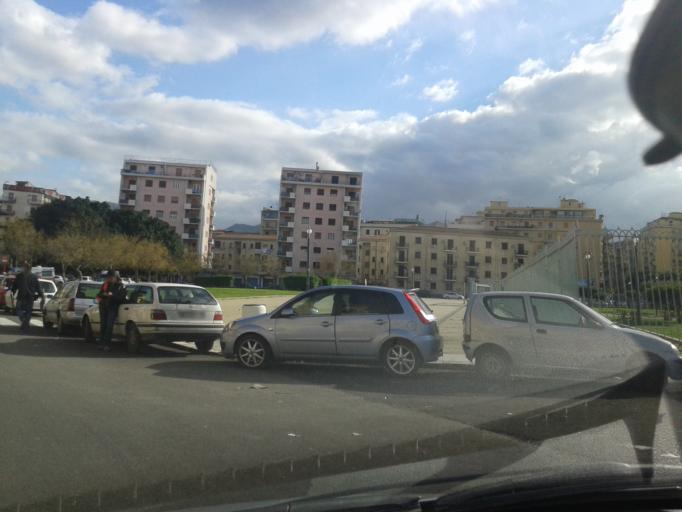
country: IT
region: Sicily
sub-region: Palermo
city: Palermo
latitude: 38.1174
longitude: 13.3438
